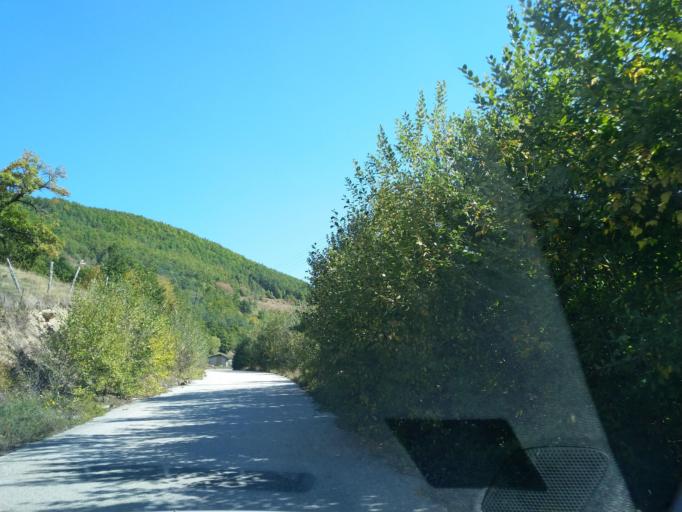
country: RS
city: Sokolovica
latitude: 43.2609
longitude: 20.2964
